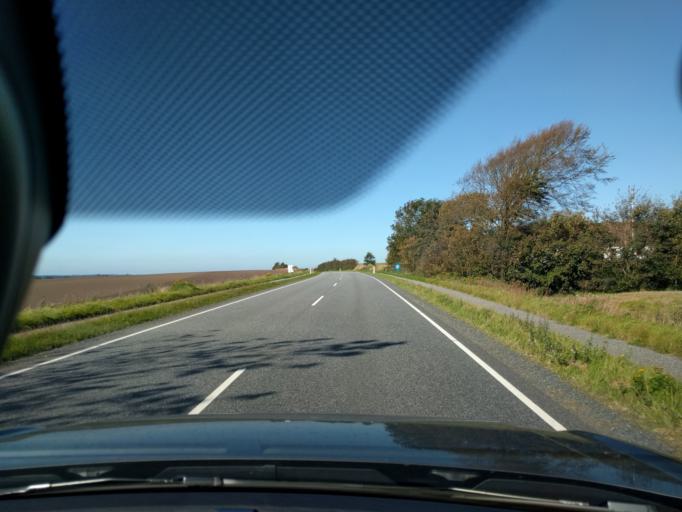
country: DK
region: North Denmark
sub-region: Vesthimmerland Kommune
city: Aars
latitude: 56.7382
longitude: 9.5998
